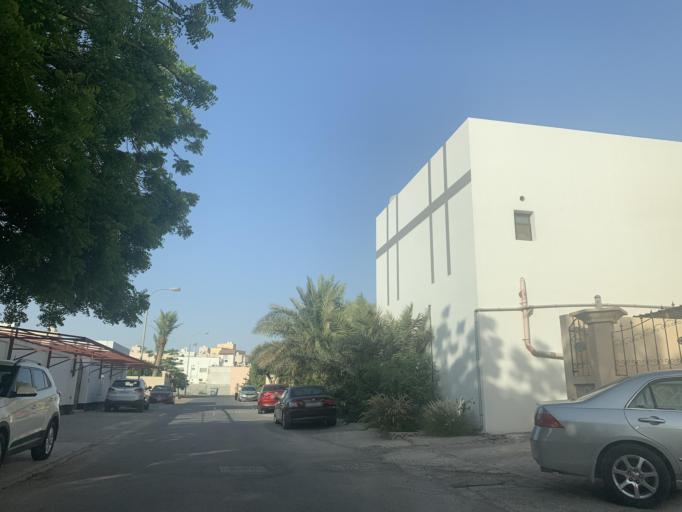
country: BH
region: Manama
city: Jidd Hafs
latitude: 26.2103
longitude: 50.5316
